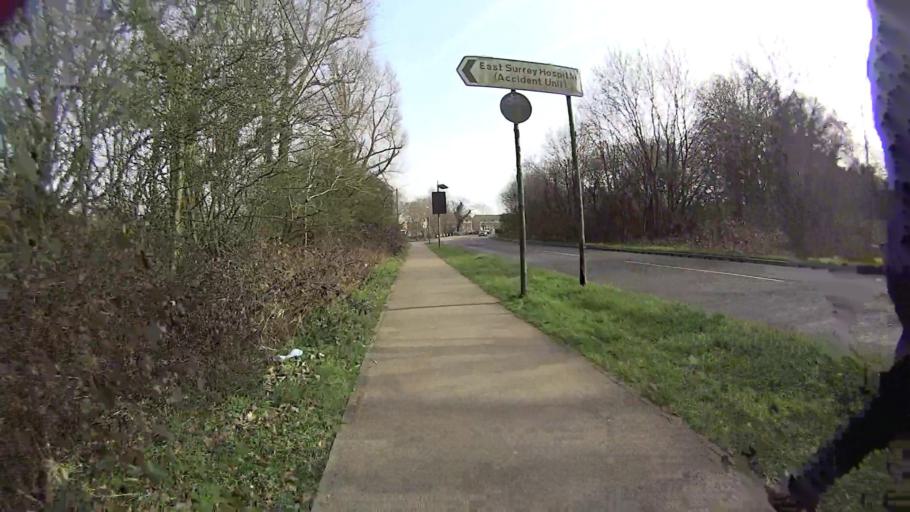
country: GB
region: England
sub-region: Surrey
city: Salfords
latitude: 51.2176
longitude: -0.1767
